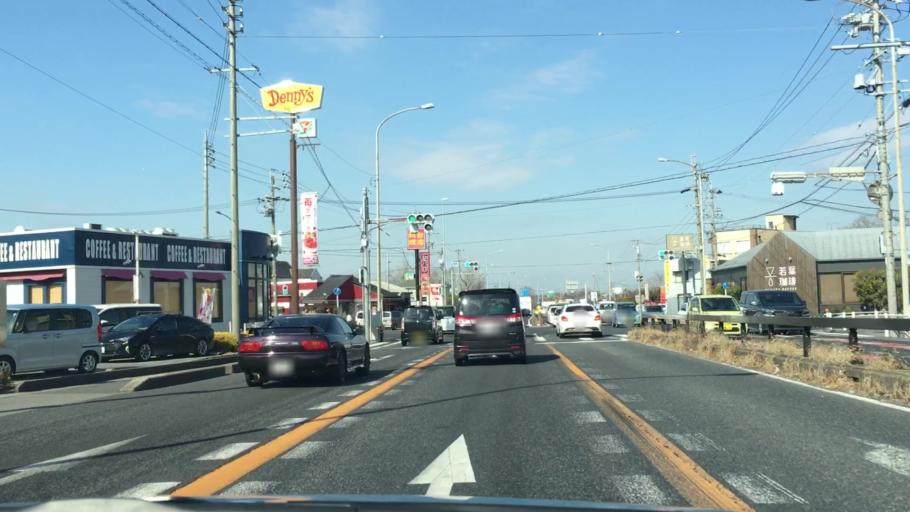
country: JP
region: Aichi
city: Okazaki
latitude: 34.9298
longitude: 137.1978
